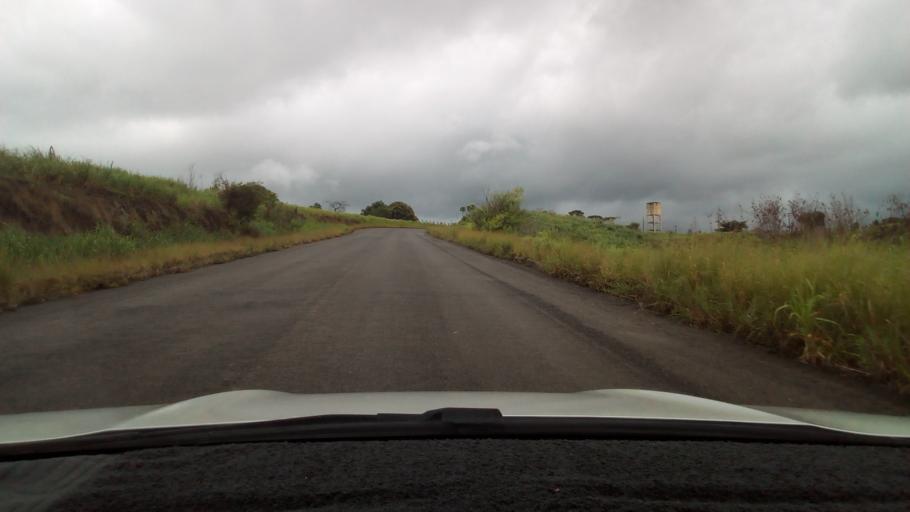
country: BR
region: Paraiba
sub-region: Pitimbu
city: Pitimbu
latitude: -7.3757
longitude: -34.8226
